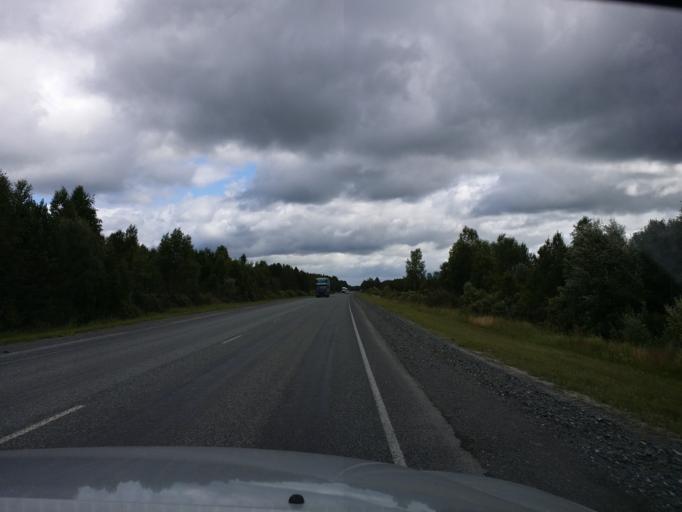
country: RU
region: Tjumen
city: Yarkovo
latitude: 57.6125
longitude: 67.3006
